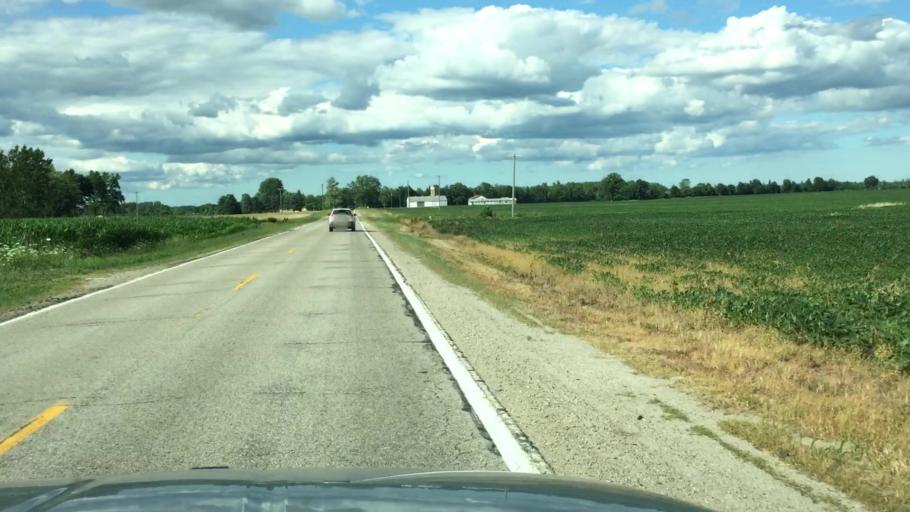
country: US
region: Michigan
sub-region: Saint Clair County
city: Capac
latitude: 43.0714
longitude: -82.9244
